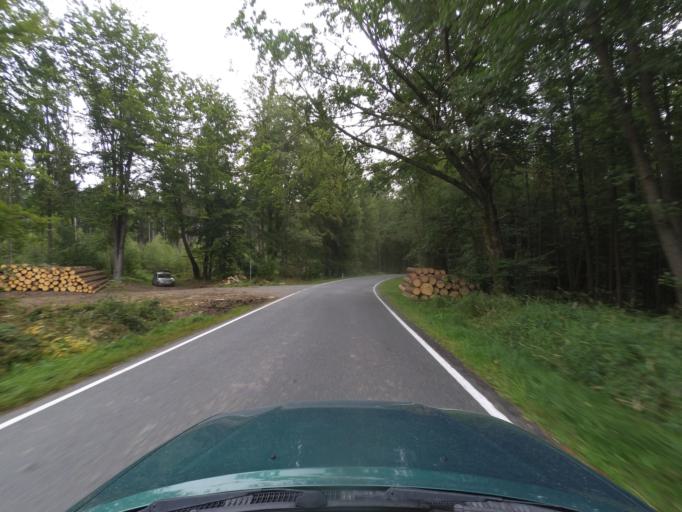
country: CZ
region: Plzensky
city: Bela nad Radbuzou
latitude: 49.5876
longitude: 12.6457
